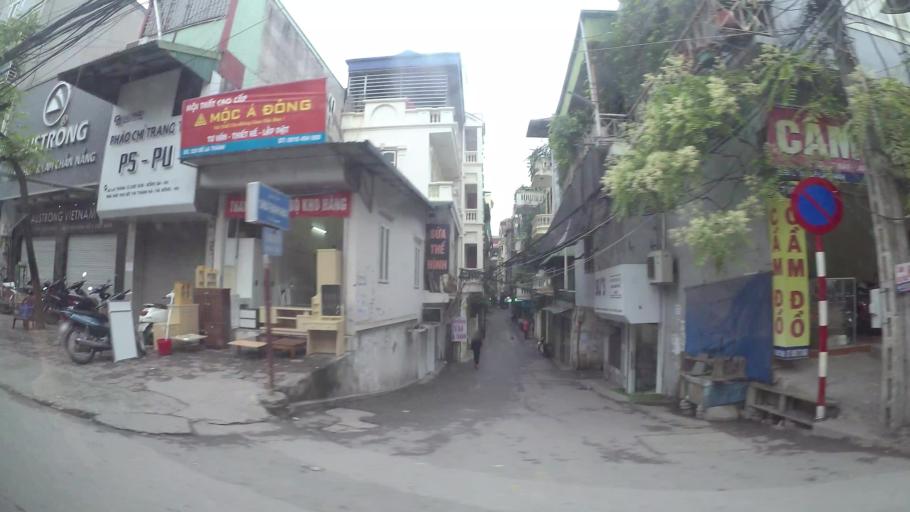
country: VN
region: Ha Noi
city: Dong Da
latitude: 21.0221
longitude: 105.8241
